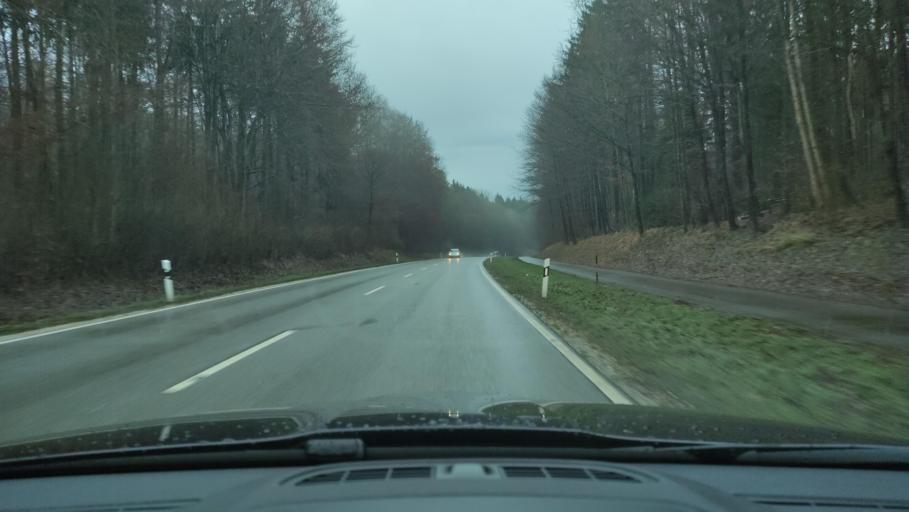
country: DE
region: Bavaria
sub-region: Swabia
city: Thannhausen
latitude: 48.2896
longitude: 10.4957
